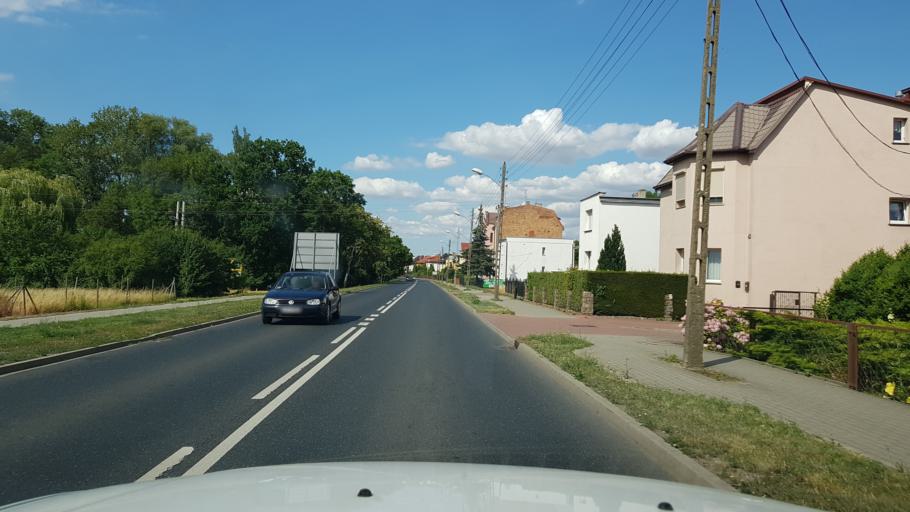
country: PL
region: West Pomeranian Voivodeship
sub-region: Powiat pyrzycki
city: Pyrzyce
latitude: 53.1326
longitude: 14.8917
